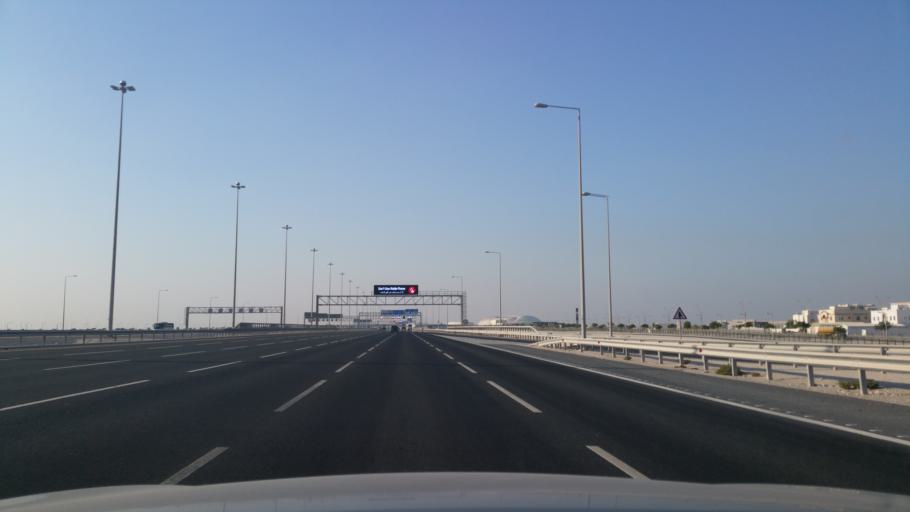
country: QA
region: Al Wakrah
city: Al Wakrah
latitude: 25.1378
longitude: 51.5831
